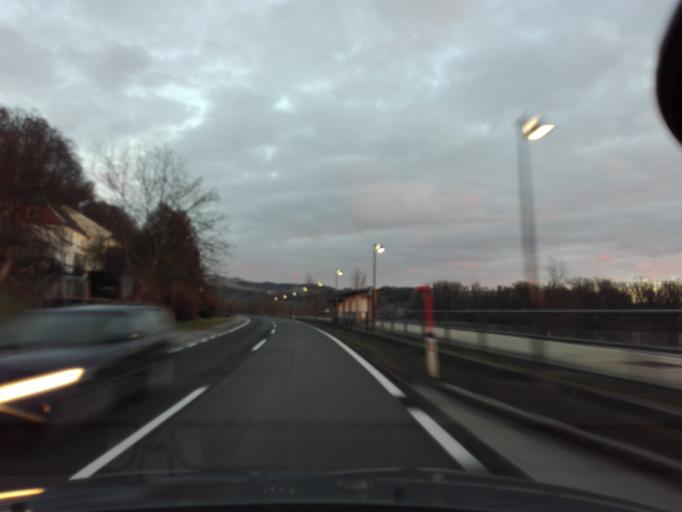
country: AT
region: Upper Austria
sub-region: Politischer Bezirk Perg
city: Bad Kreuzen
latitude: 48.1923
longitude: 14.8193
